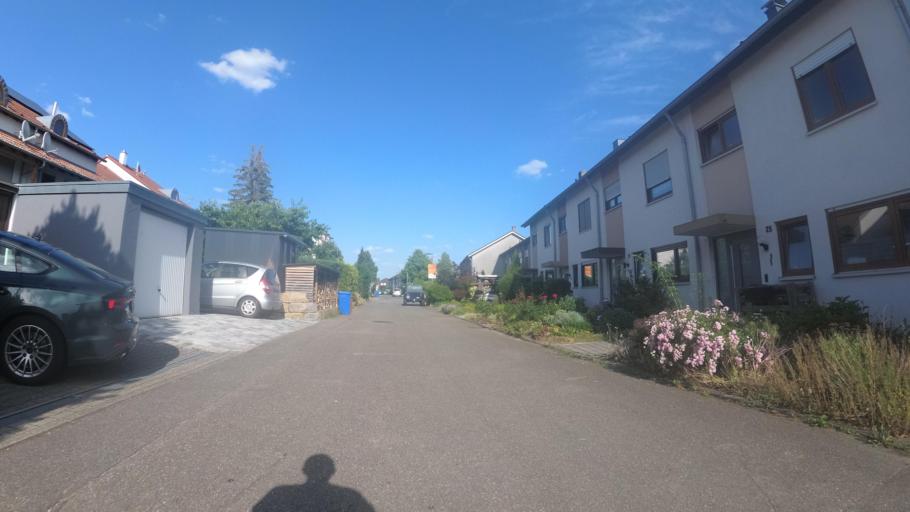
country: DE
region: Baden-Wuerttemberg
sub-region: Regierungsbezirk Stuttgart
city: Offenau
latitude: 49.2525
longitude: 9.1904
